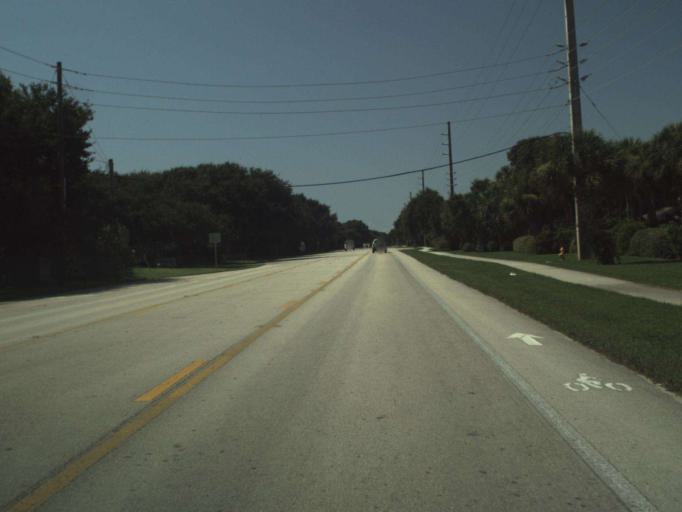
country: US
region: Florida
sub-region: Indian River County
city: Indian River Shores
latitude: 27.6909
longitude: -80.3705
